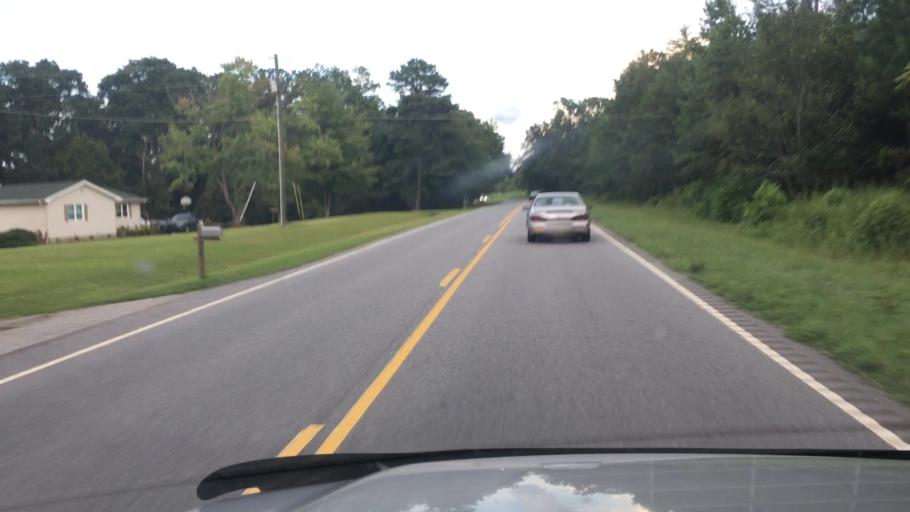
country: US
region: South Carolina
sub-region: Spartanburg County
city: Mayo
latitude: 35.1228
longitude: -81.7656
